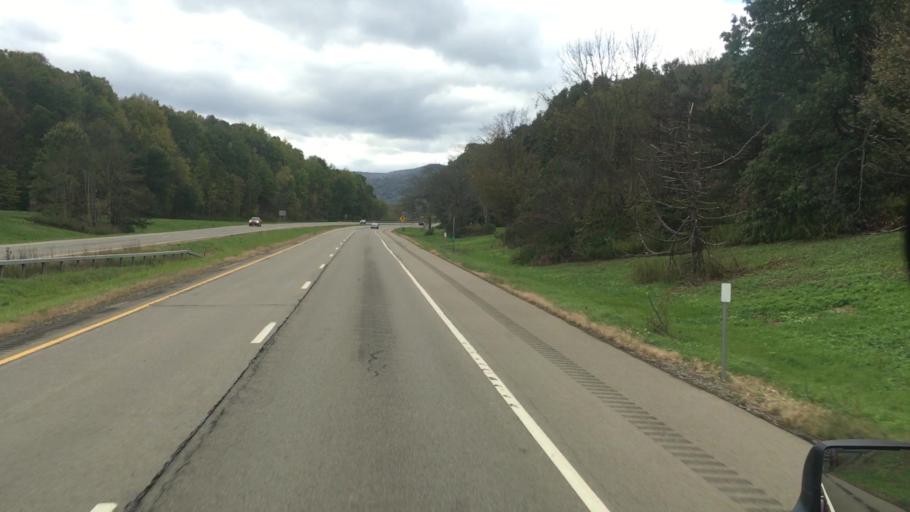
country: US
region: New York
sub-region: Cattaraugus County
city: Randolph
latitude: 42.0995
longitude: -78.8484
